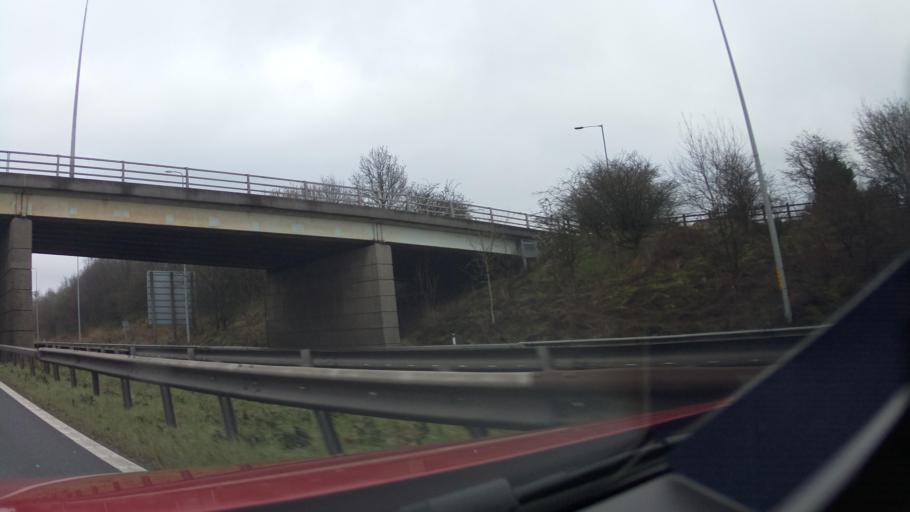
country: GB
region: England
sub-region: Borough of Wigan
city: Shevington
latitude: 53.5949
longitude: -2.6936
